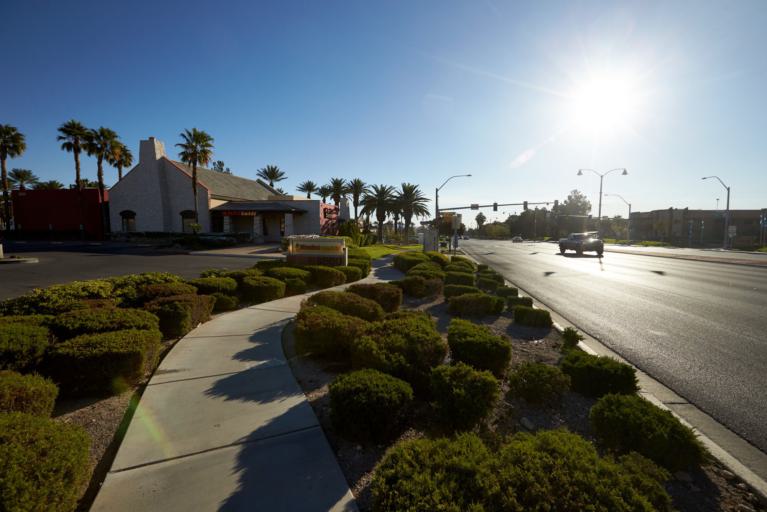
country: US
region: Nevada
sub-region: Clark County
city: Summerlin South
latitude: 36.1446
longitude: -115.3032
